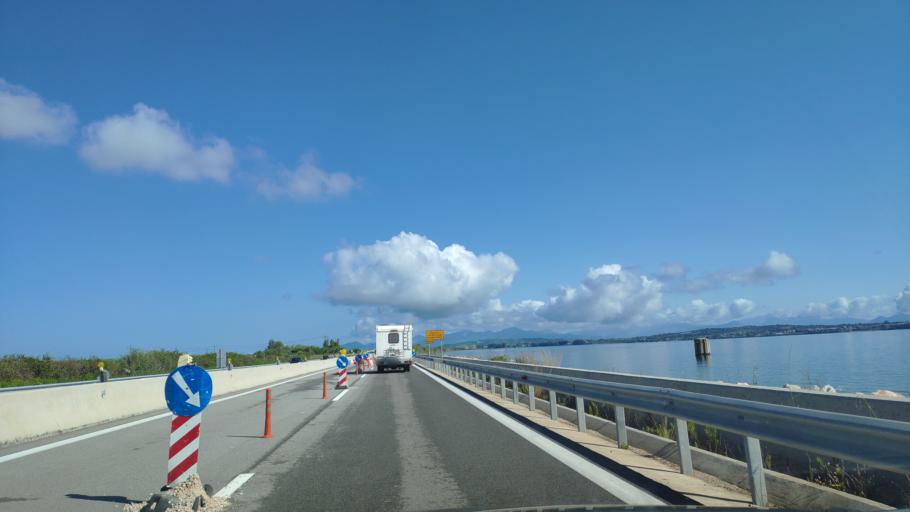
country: GR
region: Epirus
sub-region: Nomos Prevezis
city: Preveza
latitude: 38.9295
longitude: 20.7826
